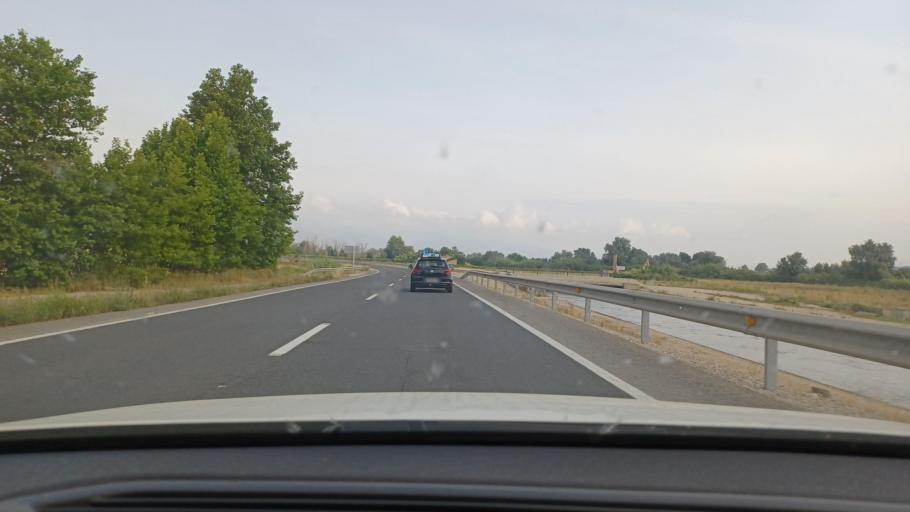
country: ES
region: Catalonia
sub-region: Provincia de Tarragona
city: Tortosa
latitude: 40.7728
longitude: 0.5280
